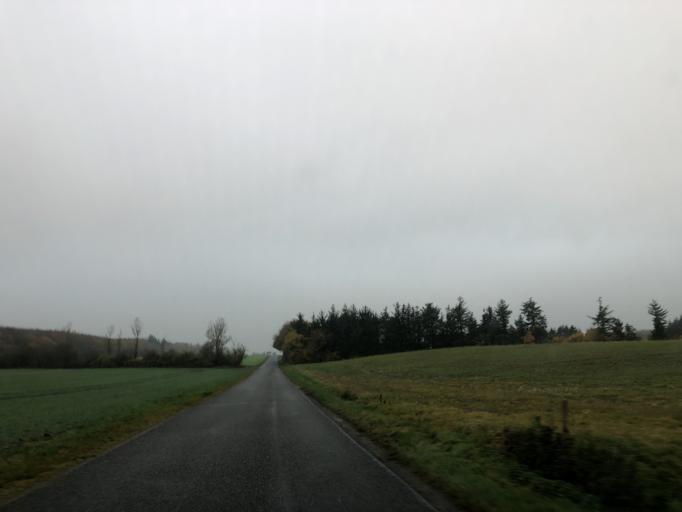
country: DK
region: Central Jutland
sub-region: Herning Kommune
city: Vildbjerg
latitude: 56.2021
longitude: 8.6848
